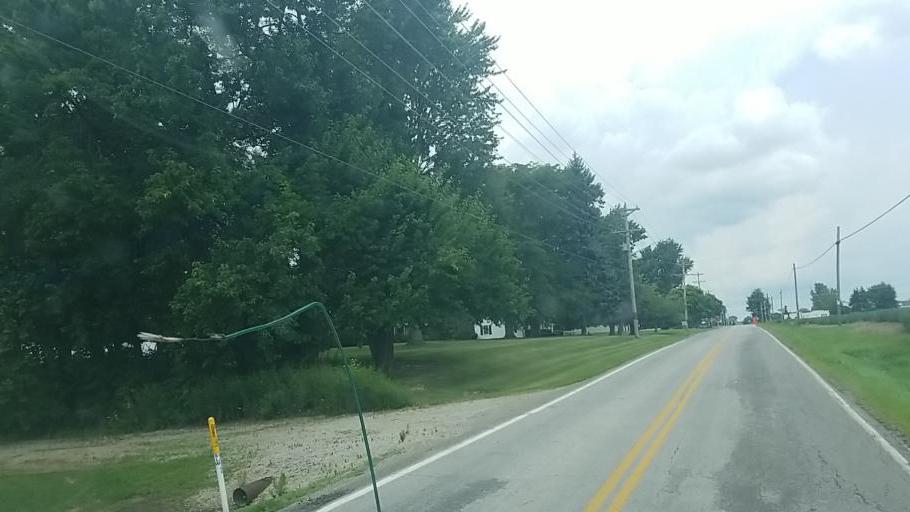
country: US
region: Ohio
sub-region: Lorain County
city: Wellington
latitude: 41.1665
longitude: -82.1692
